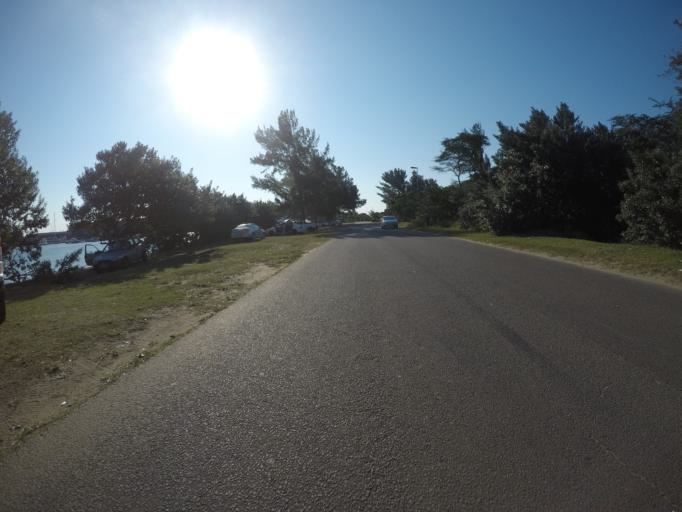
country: ZA
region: KwaZulu-Natal
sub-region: uThungulu District Municipality
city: Richards Bay
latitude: -28.7955
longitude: 32.0818
